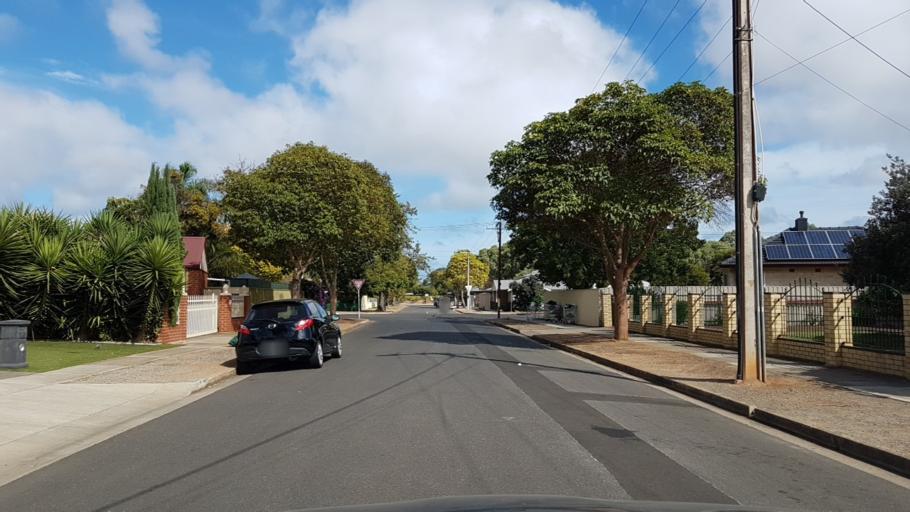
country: AU
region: South Australia
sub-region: Marion
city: Plympton Park
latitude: -34.9945
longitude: 138.5521
